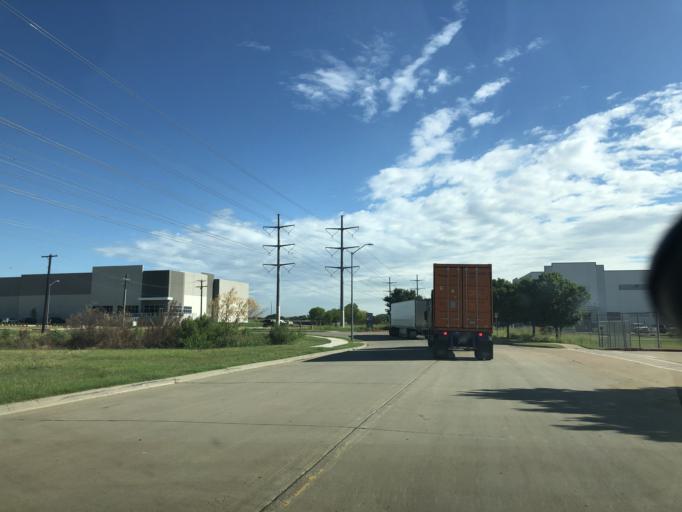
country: US
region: Texas
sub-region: Tarrant County
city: Euless
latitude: 32.8201
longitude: -97.0246
